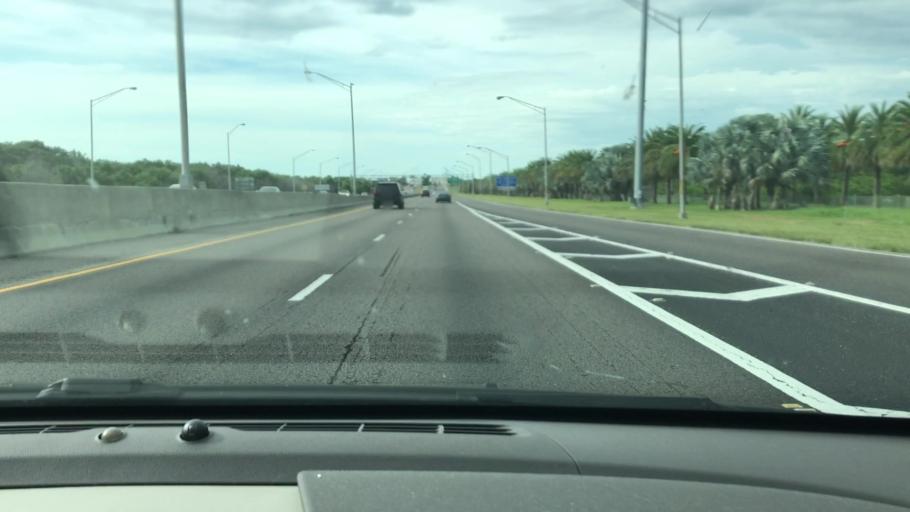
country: US
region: Florida
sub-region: Pinellas County
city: Tierra Verde
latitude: 27.6822
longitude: -82.6780
